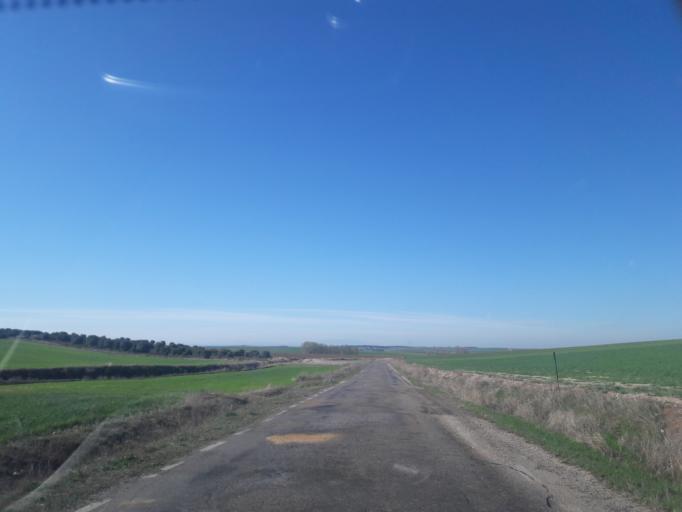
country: ES
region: Castille and Leon
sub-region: Provincia de Salamanca
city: Tordillos
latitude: 40.8674
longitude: -5.3355
